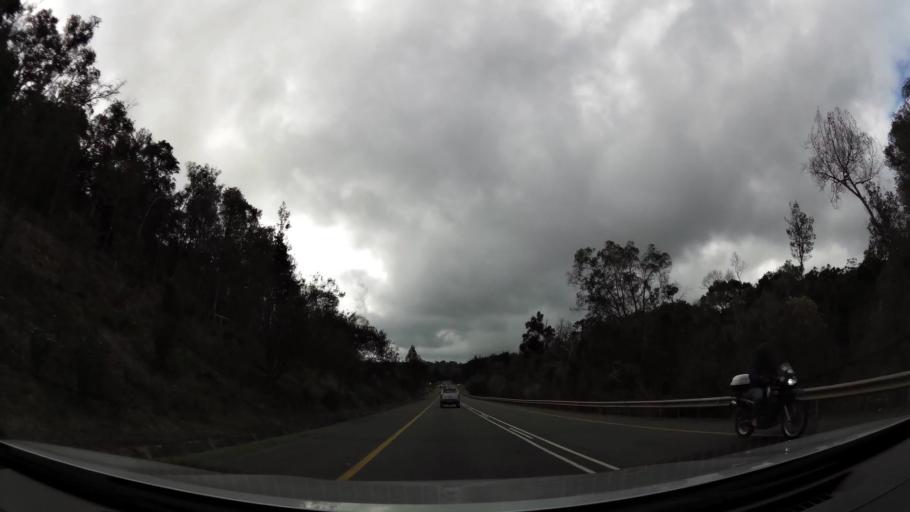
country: ZA
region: Western Cape
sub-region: Eden District Municipality
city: Knysna
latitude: -34.0327
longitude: 23.1586
